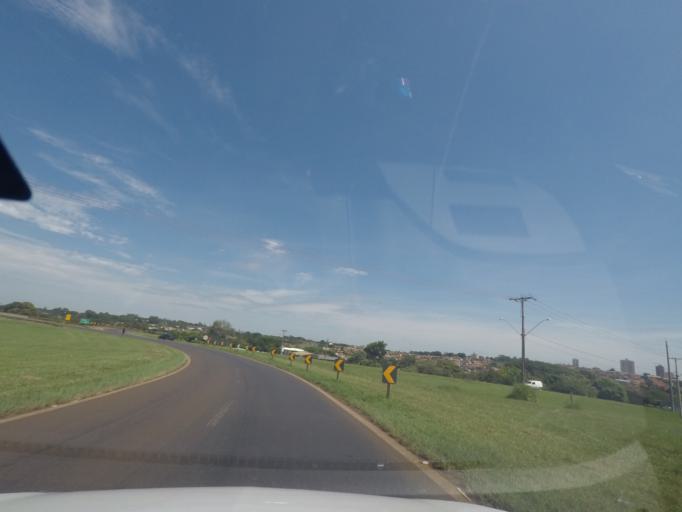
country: BR
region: Sao Paulo
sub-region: Araraquara
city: Araraquara
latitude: -21.8170
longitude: -48.1783
